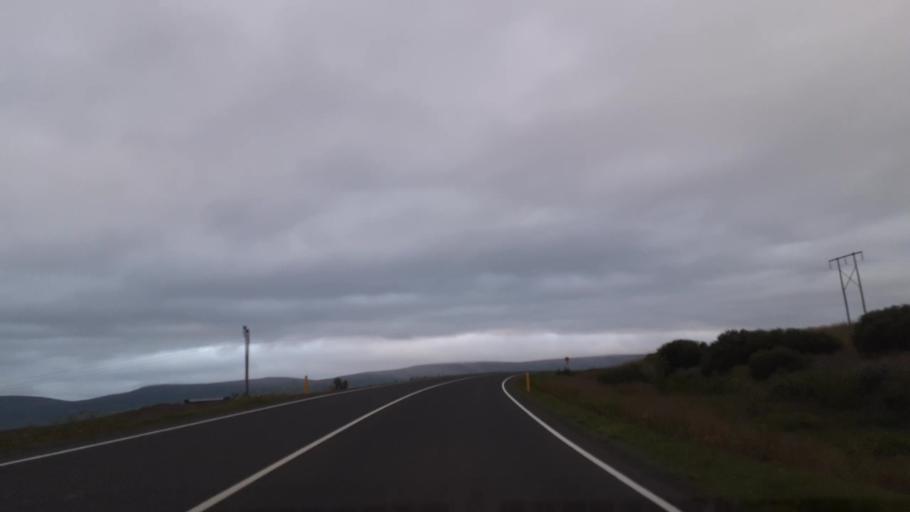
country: IS
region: Northeast
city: Akureyri
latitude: 65.7477
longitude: -18.2157
